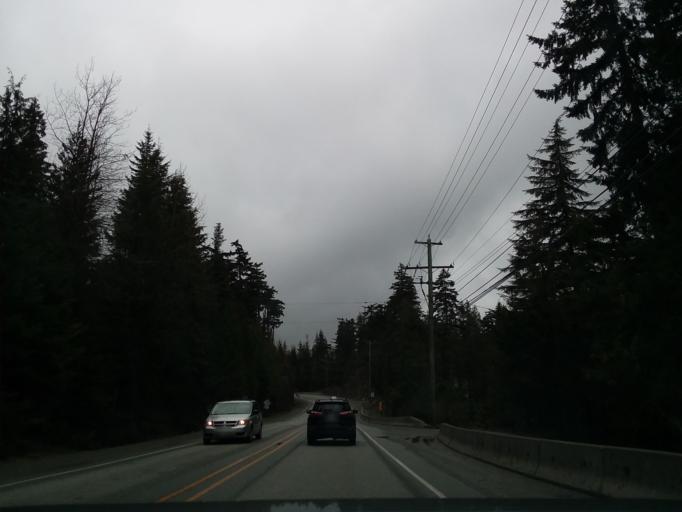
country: CA
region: British Columbia
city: Whistler
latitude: 50.1030
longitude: -122.9882
